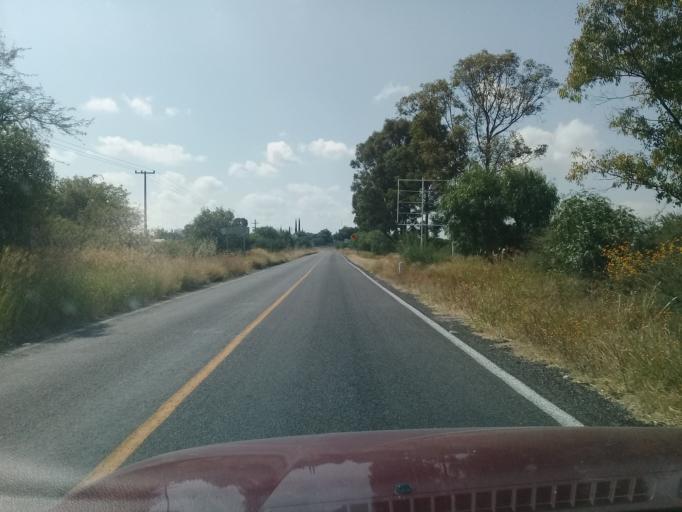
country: MX
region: Aguascalientes
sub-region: Aguascalientes
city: Penuelas (El Cienegal)
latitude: 21.7132
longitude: -102.3724
